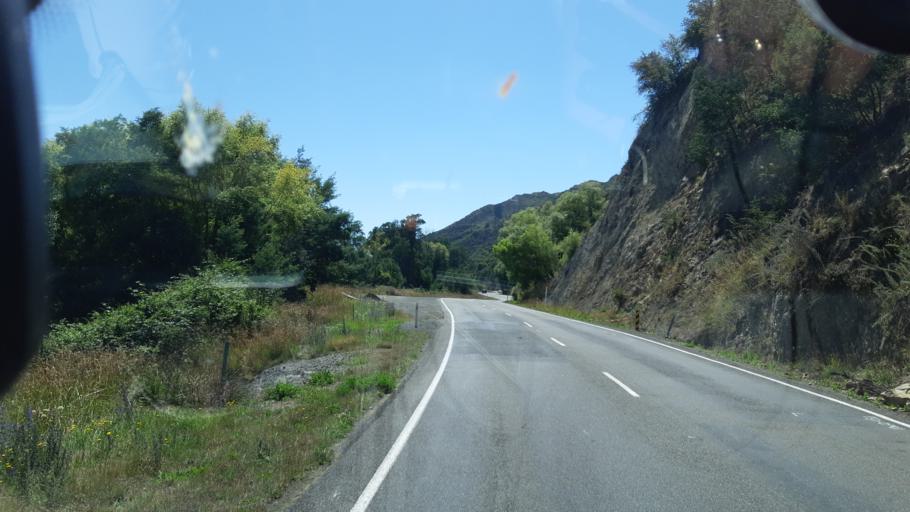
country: NZ
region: Canterbury
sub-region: Kaikoura District
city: Kaikoura
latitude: -42.6355
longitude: 173.3468
